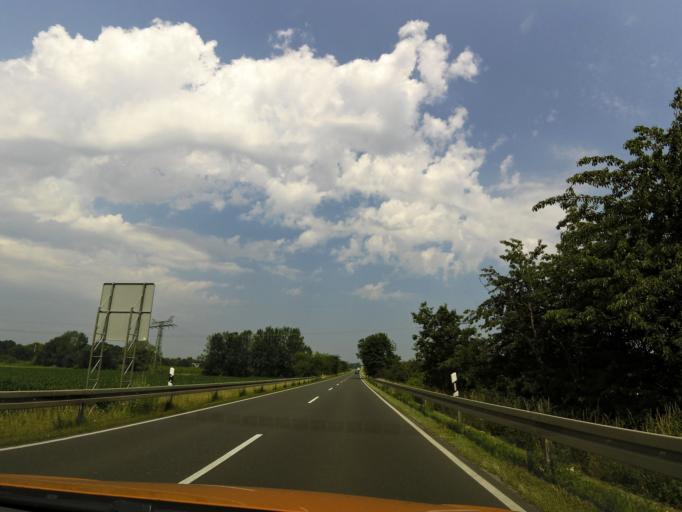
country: DE
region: Brandenburg
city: Werder
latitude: 52.4547
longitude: 12.9781
